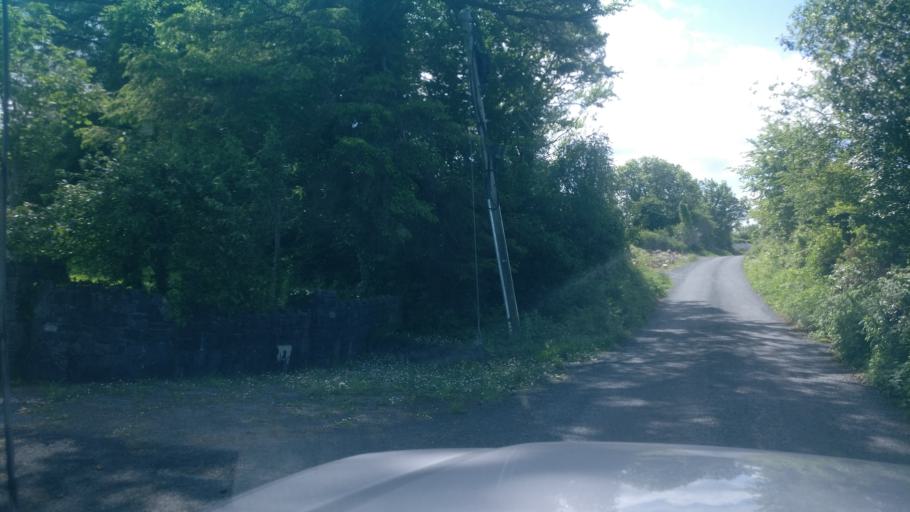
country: IE
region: Connaught
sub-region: County Galway
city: Gort
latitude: 53.1296
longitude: -8.7062
